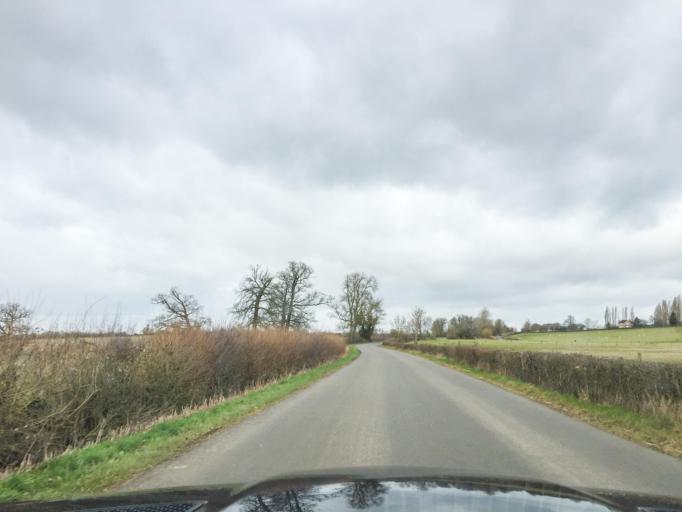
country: GB
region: England
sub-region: Warwickshire
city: Shipston on Stour
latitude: 52.0824
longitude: -1.6037
